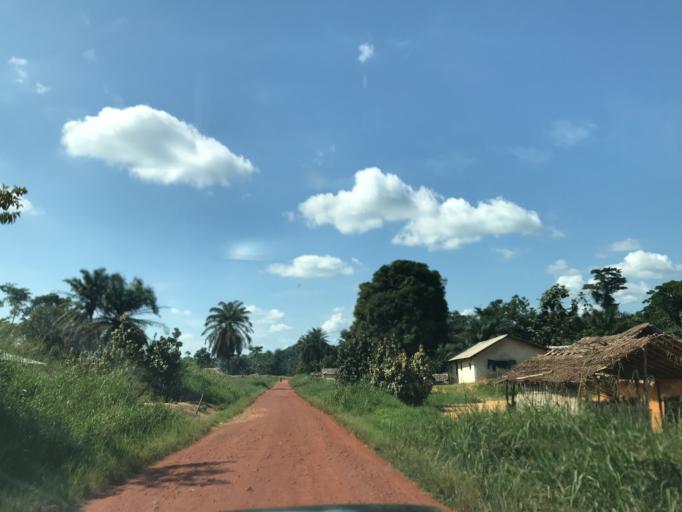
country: CD
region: Eastern Province
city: Kisangani
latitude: 1.1995
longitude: 25.2572
